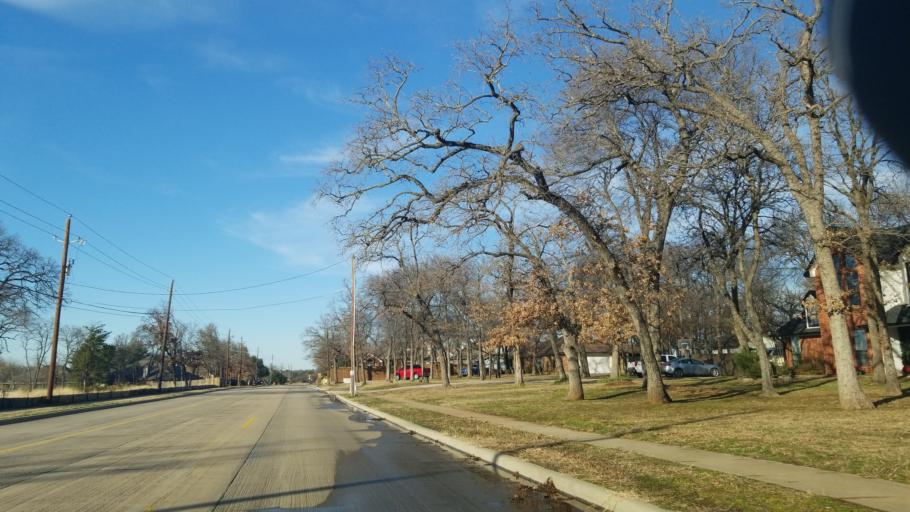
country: US
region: Texas
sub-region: Denton County
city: Corinth
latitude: 33.1390
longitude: -97.0652
